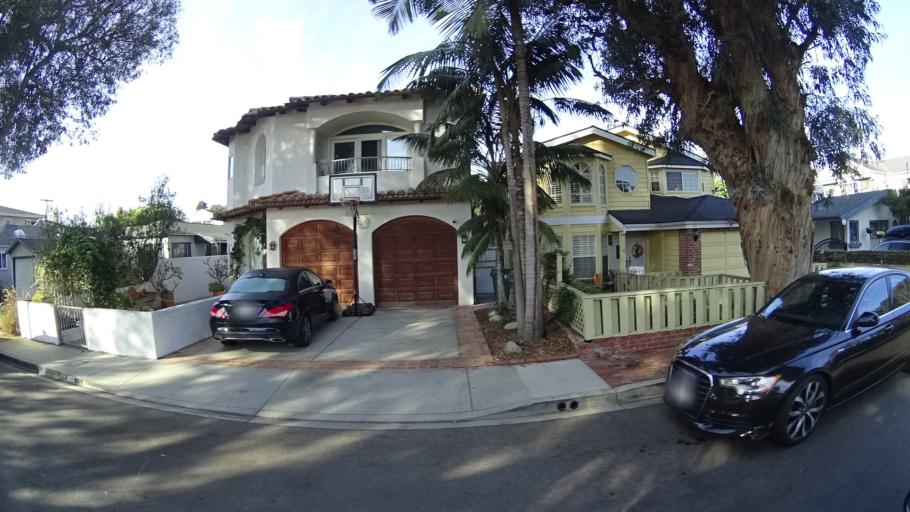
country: US
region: California
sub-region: Los Angeles County
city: Manhattan Beach
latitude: 33.8917
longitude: -118.4043
